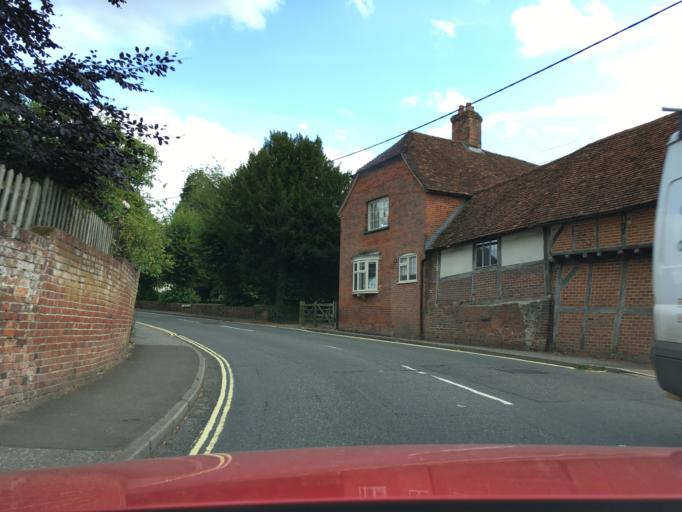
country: GB
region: England
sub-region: Hampshire
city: Kingsclere
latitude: 51.3252
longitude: -1.2482
